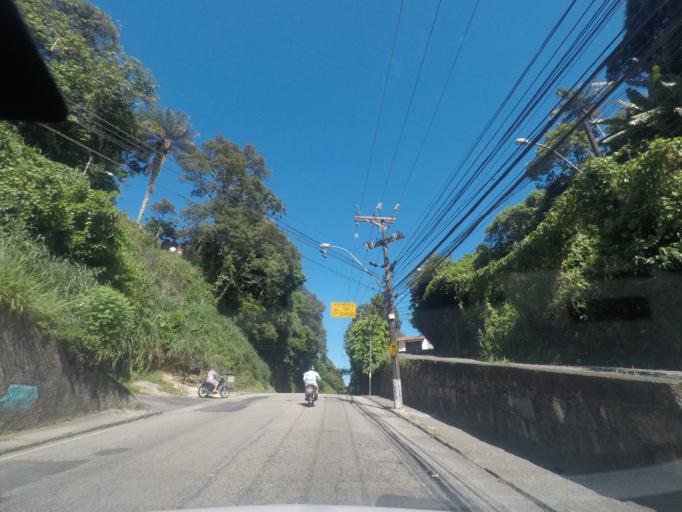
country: BR
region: Rio de Janeiro
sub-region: Petropolis
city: Petropolis
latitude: -22.5273
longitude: -43.1787
